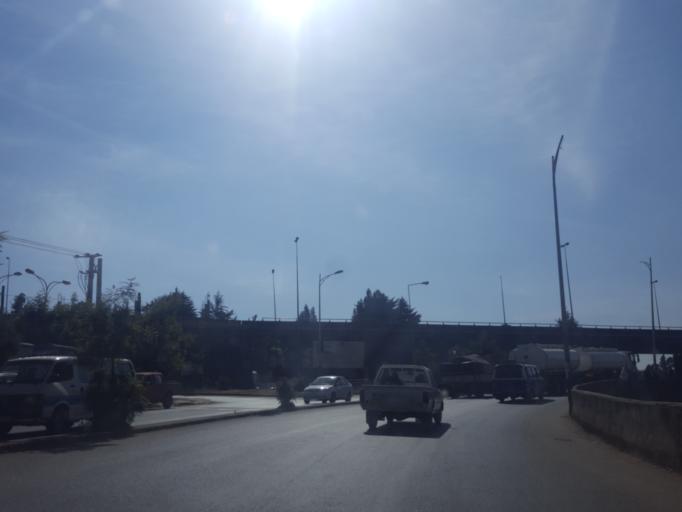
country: ET
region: Adis Abeba
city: Addis Ababa
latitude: 9.0579
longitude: 38.7128
